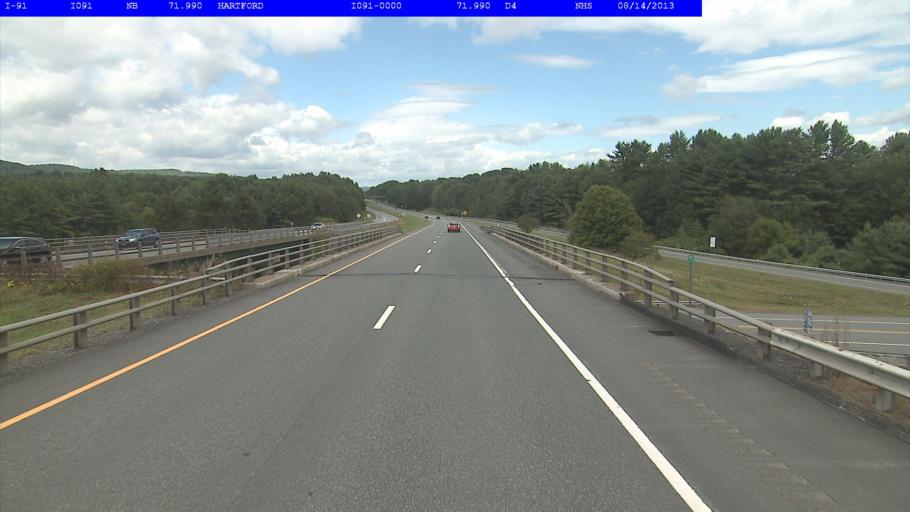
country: US
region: Vermont
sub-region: Windsor County
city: Wilder
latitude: 43.6659
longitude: -72.3191
